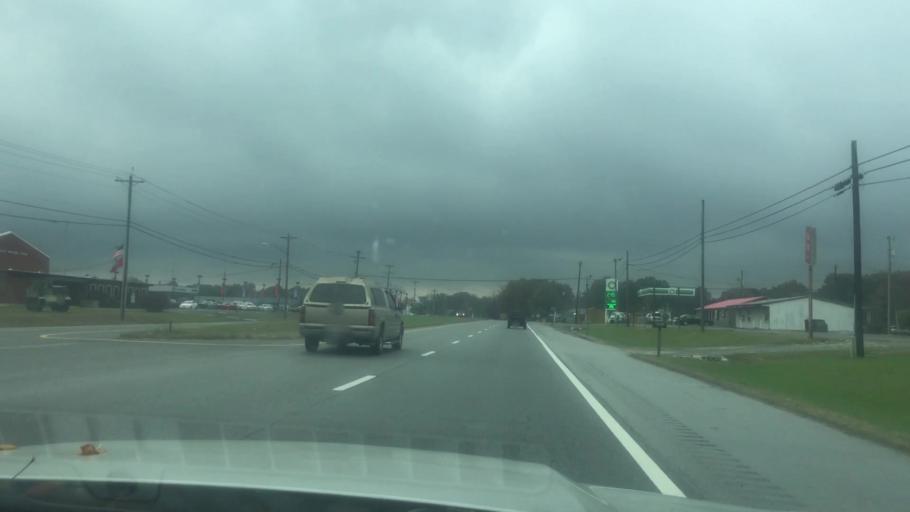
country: US
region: Tennessee
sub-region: Coffee County
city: Tullahoma
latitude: 35.3676
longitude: -86.1897
